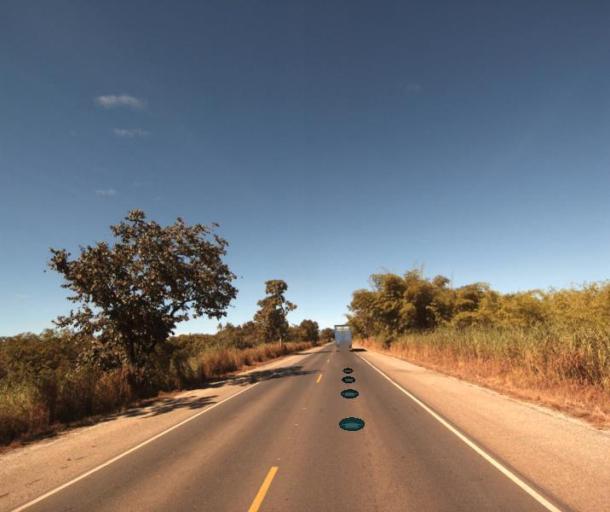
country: BR
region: Goias
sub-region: Itapaci
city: Itapaci
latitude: -14.9417
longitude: -49.3722
